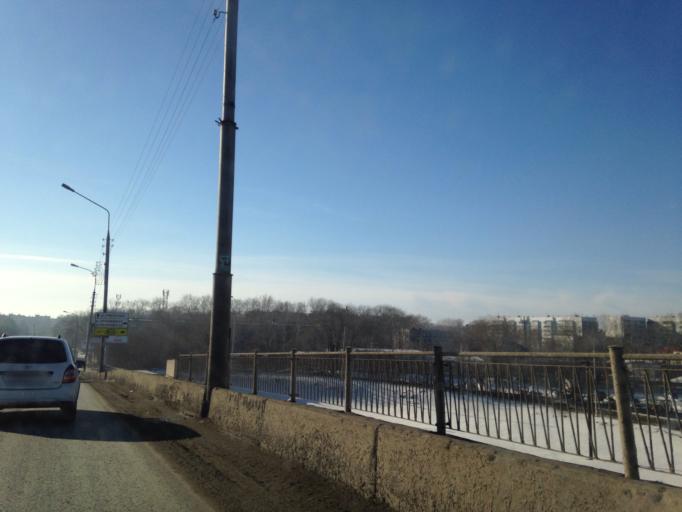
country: RU
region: Ulyanovsk
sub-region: Ulyanovskiy Rayon
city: Ulyanovsk
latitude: 54.2934
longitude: 48.3146
